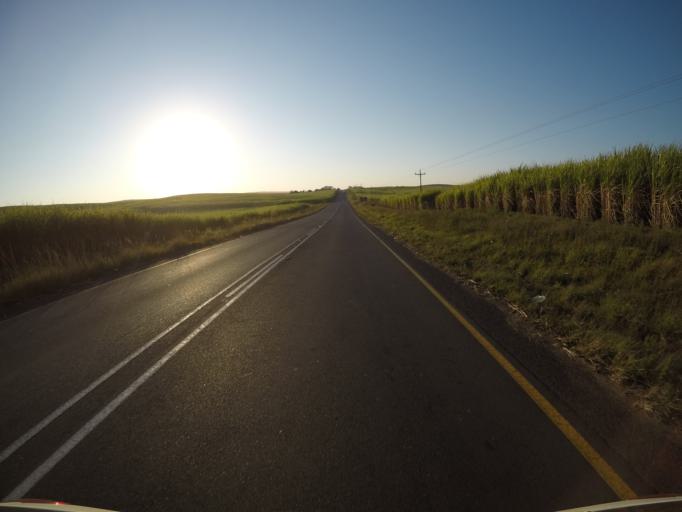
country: ZA
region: KwaZulu-Natal
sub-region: uThungulu District Municipality
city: eSikhawini
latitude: -28.9482
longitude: 31.7267
